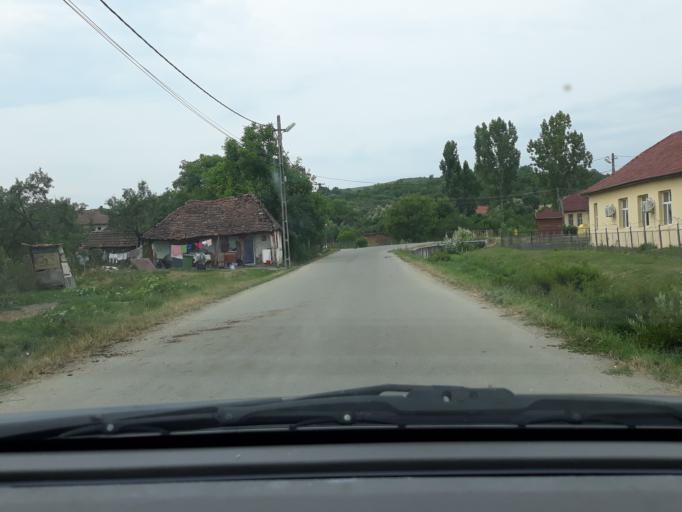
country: RO
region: Salaj
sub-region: Comuna Criseni
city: Criseni
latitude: 47.2577
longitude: 23.0629
